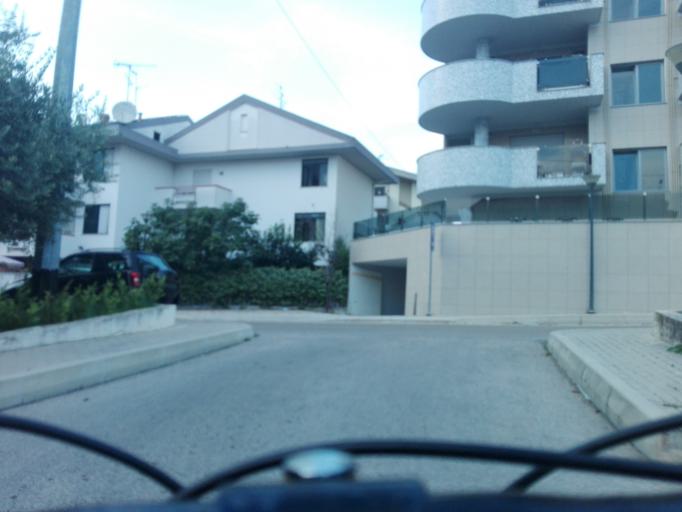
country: IT
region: Abruzzo
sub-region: Provincia di Pescara
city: Montesilvano Marina
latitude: 42.5078
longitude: 14.1451
